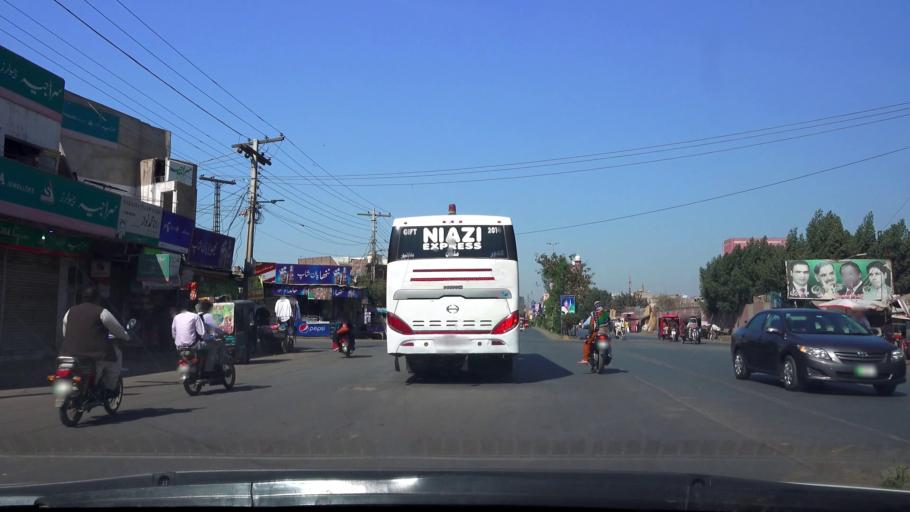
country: PK
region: Punjab
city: Faisalabad
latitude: 31.4119
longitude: 73.0749
